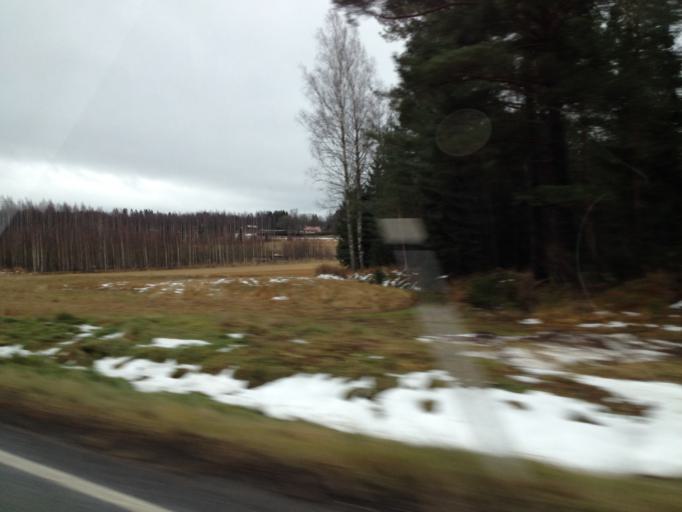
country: FI
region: Uusimaa
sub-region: Raaseporin
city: Ekenaes
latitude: 59.9562
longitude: 23.3661
